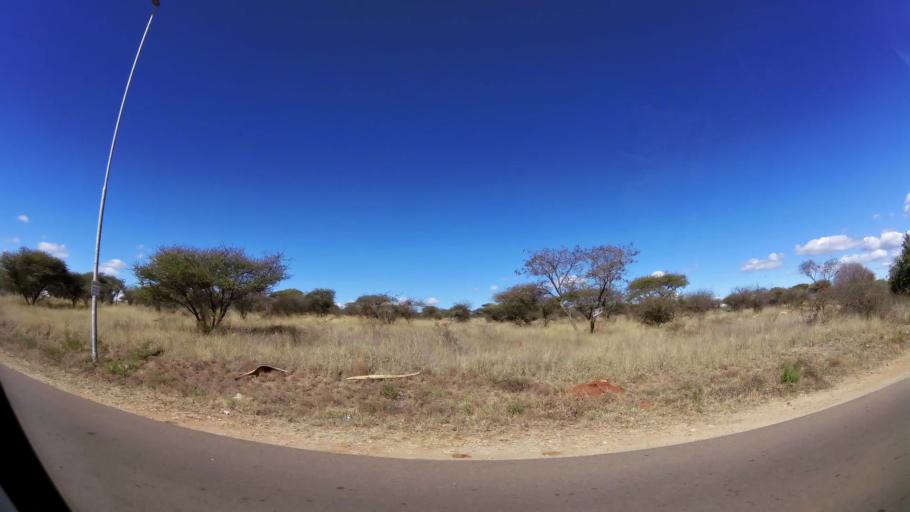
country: ZA
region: Limpopo
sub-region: Capricorn District Municipality
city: Polokwane
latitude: -23.8823
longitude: 29.5107
